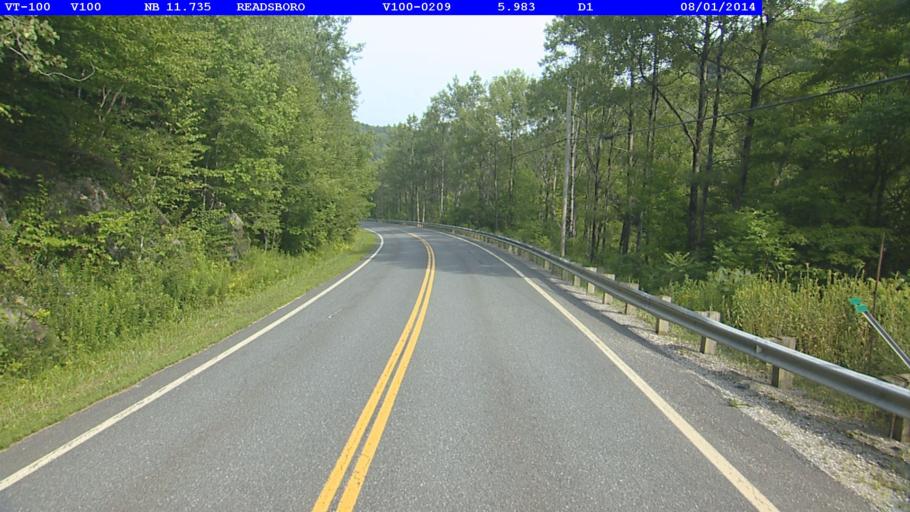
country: US
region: Massachusetts
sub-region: Berkshire County
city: North Adams
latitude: 42.7816
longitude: -72.9590
